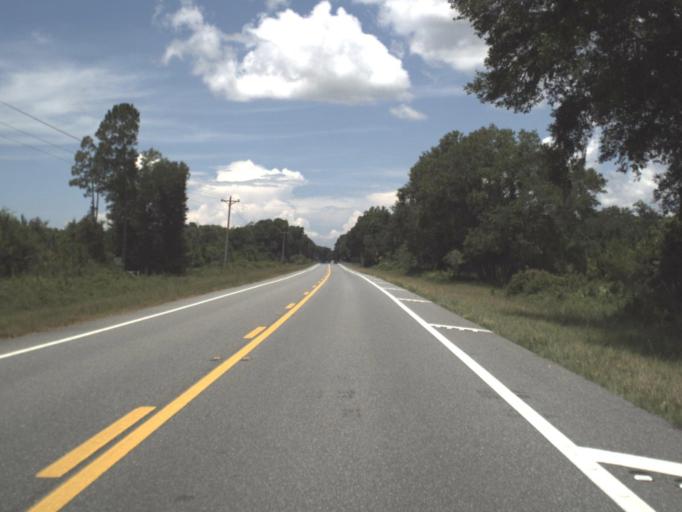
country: US
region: Florida
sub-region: Taylor County
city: Perry
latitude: 30.1428
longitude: -83.8615
